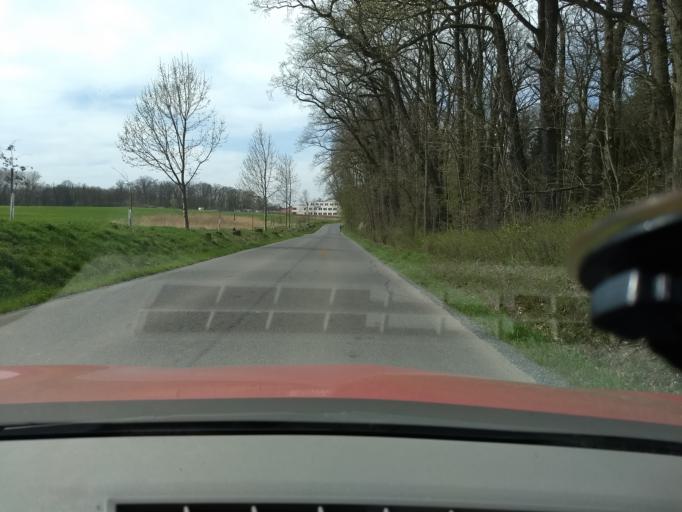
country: CZ
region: Central Bohemia
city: Hostivice
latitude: 50.0683
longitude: 14.2540
